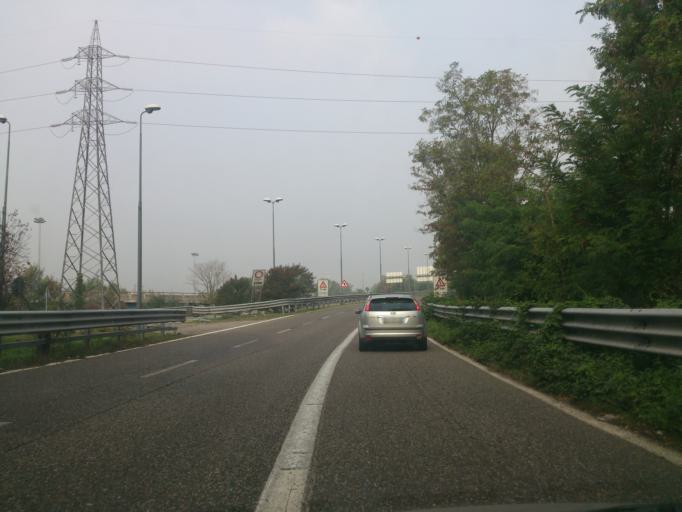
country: IT
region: Lombardy
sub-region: Citta metropolitana di Milano
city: Chiaravalle
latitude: 45.4274
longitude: 9.2454
